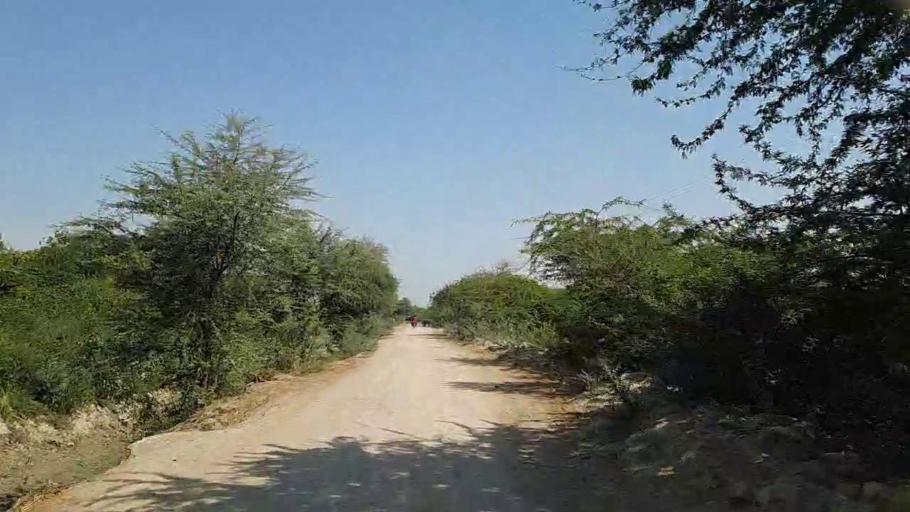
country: PK
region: Sindh
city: Mirpur Batoro
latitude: 24.6904
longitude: 68.2577
